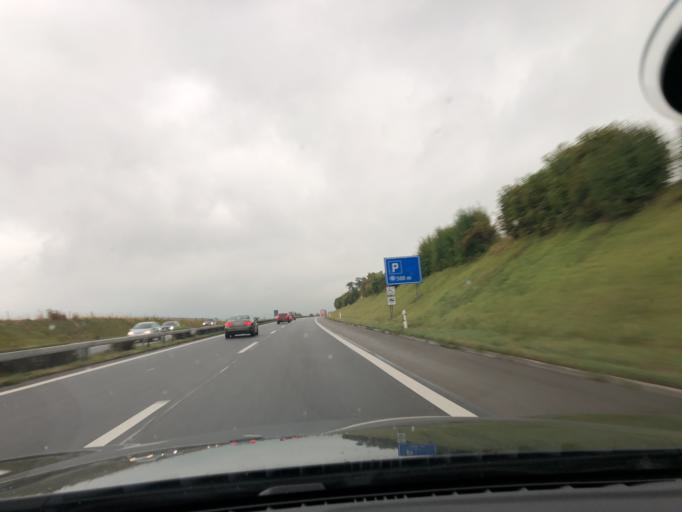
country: CH
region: Zurich
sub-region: Bezirk Horgen
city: Waedenswil / Leihof-Muehlebach
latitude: 47.2176
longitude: 8.6655
